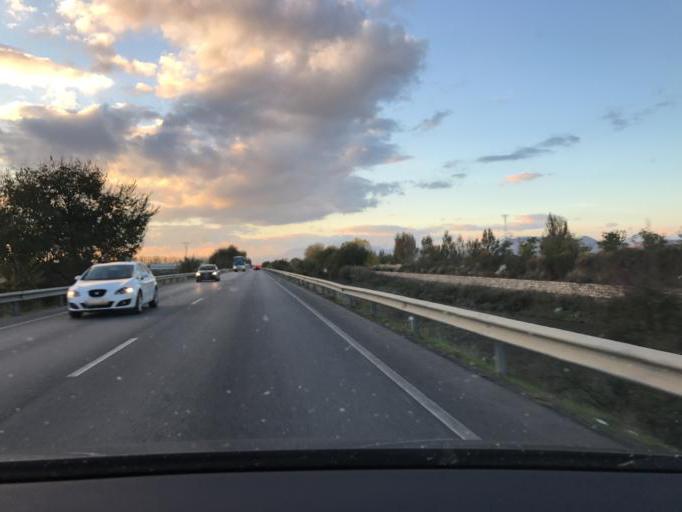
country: ES
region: Andalusia
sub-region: Provincia de Granada
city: Churriana de la Vega
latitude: 37.1650
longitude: -3.6332
